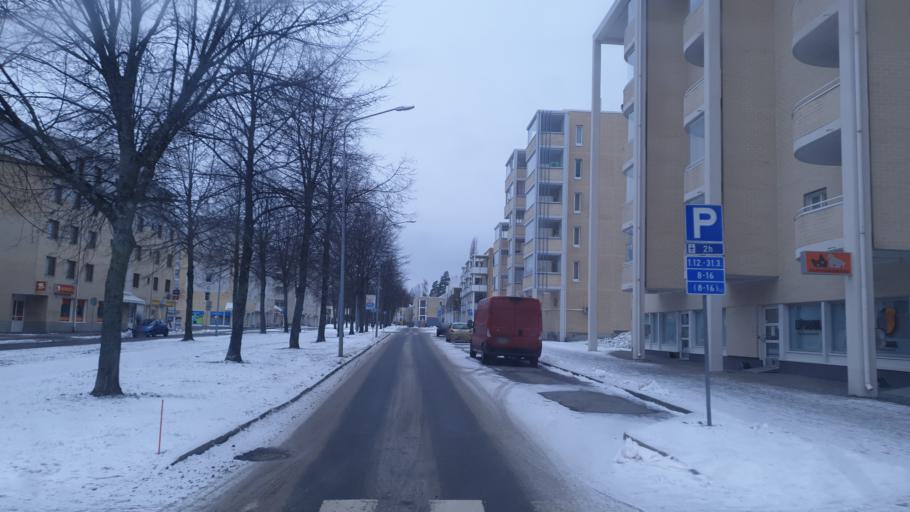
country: FI
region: Northern Savo
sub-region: Kuopio
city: Kuopio
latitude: 62.8390
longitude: 27.6398
